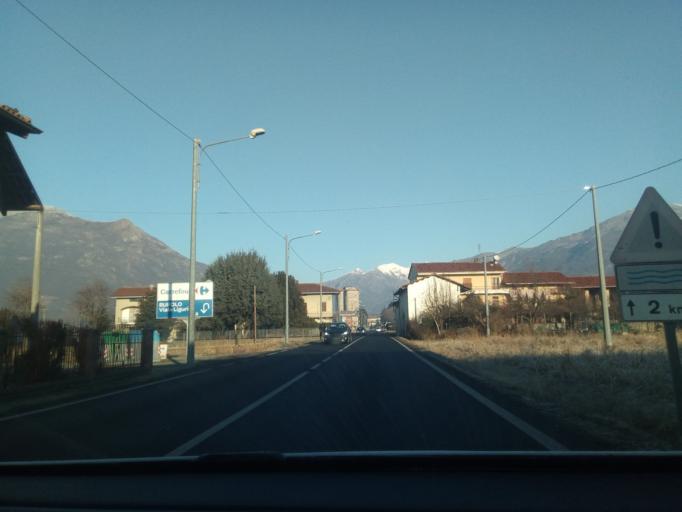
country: IT
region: Piedmont
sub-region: Provincia di Torino
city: Montalto Dora
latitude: 45.4783
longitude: 7.8655
